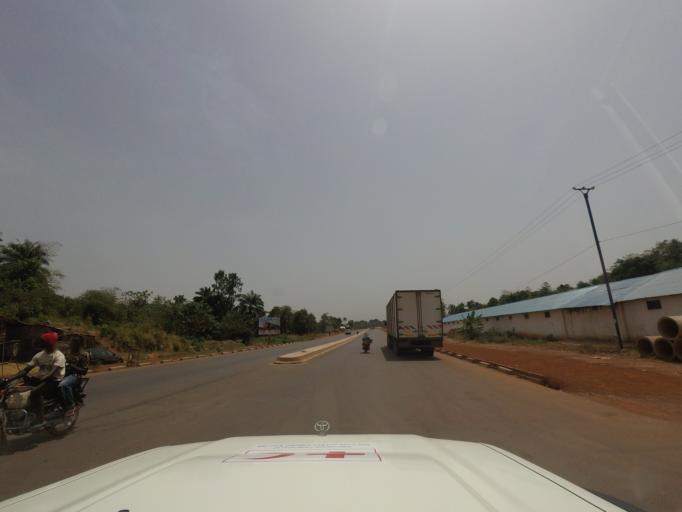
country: GN
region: Kindia
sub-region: Coyah
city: Coyah
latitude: 9.7166
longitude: -13.3743
